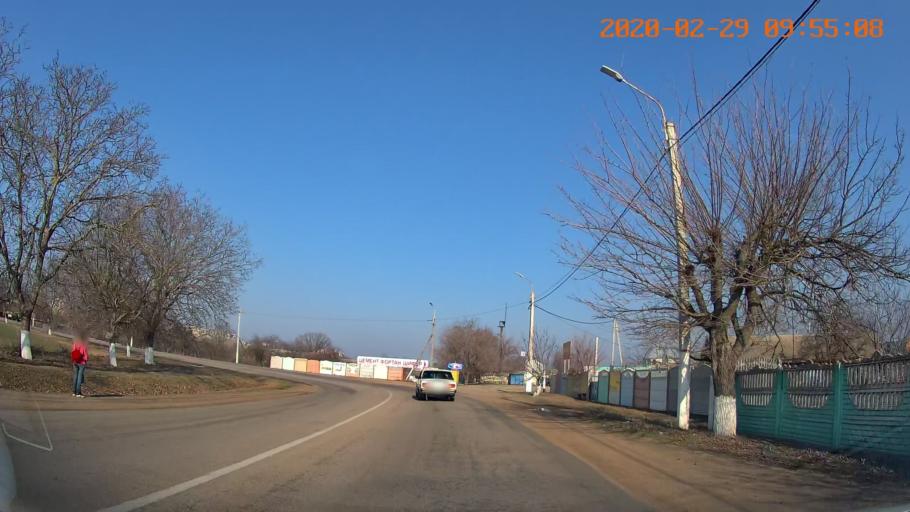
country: MD
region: Telenesti
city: Slobozia
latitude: 46.7333
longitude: 29.7119
